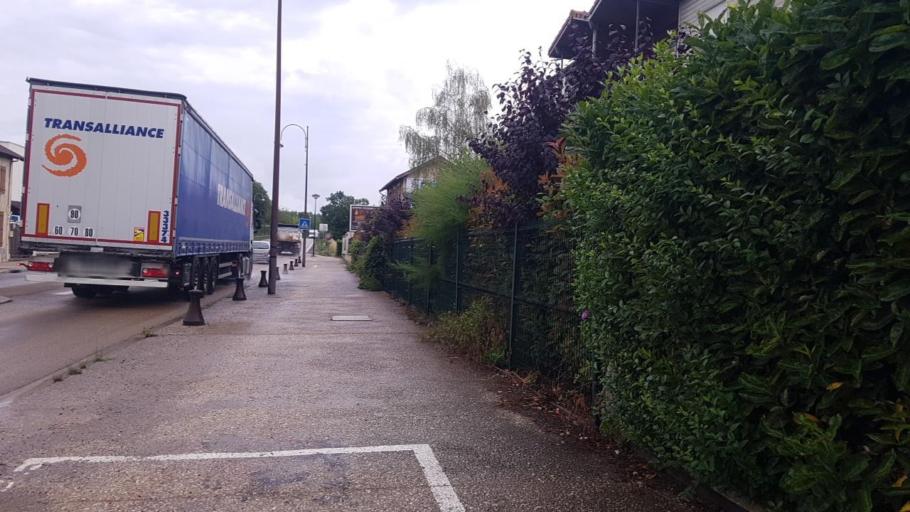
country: FR
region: Champagne-Ardenne
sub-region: Departement de la Marne
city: Vitry-le-Francois
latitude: 48.7336
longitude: 4.5898
